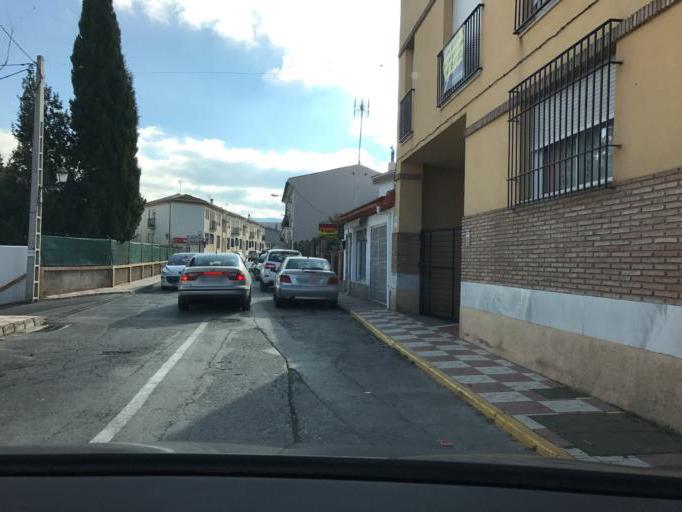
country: ES
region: Andalusia
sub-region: Provincia de Granada
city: Otura
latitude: 37.0928
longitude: -3.6372
